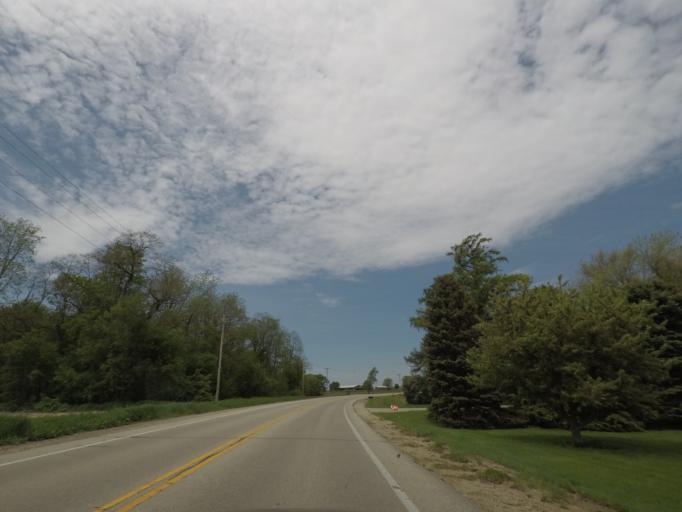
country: US
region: Wisconsin
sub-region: Rock County
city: Evansville
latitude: 42.8314
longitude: -89.3151
